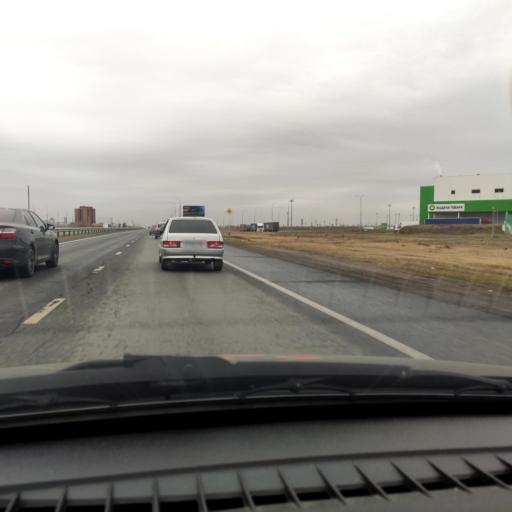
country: RU
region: Samara
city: Tol'yatti
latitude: 53.5509
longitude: 49.3357
